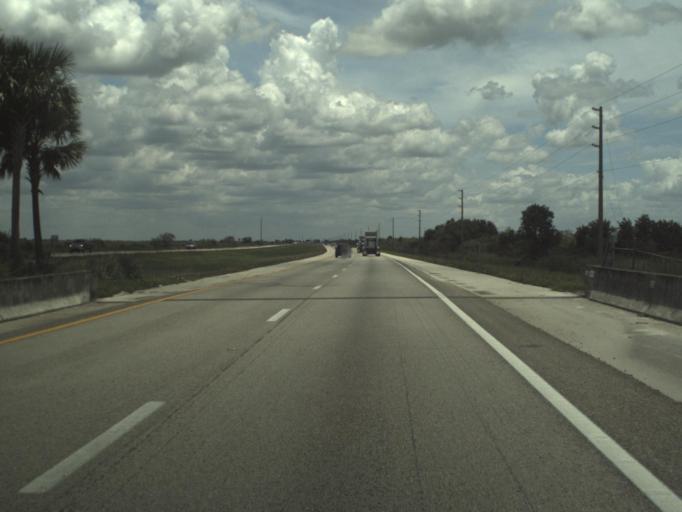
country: US
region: Florida
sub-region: Broward County
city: Weston
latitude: 26.1465
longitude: -80.7004
